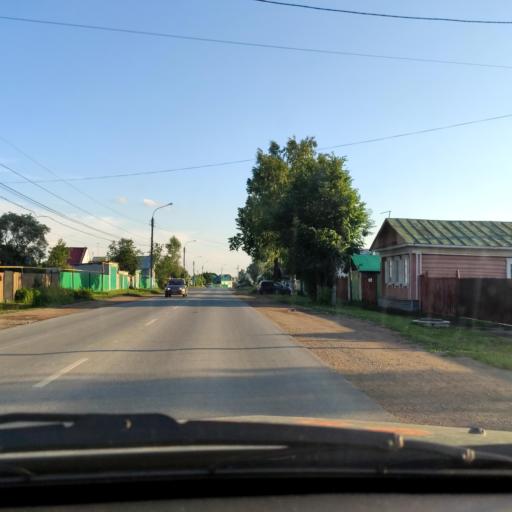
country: RU
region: Bashkortostan
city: Blagoveshchensk
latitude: 55.0341
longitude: 55.9911
